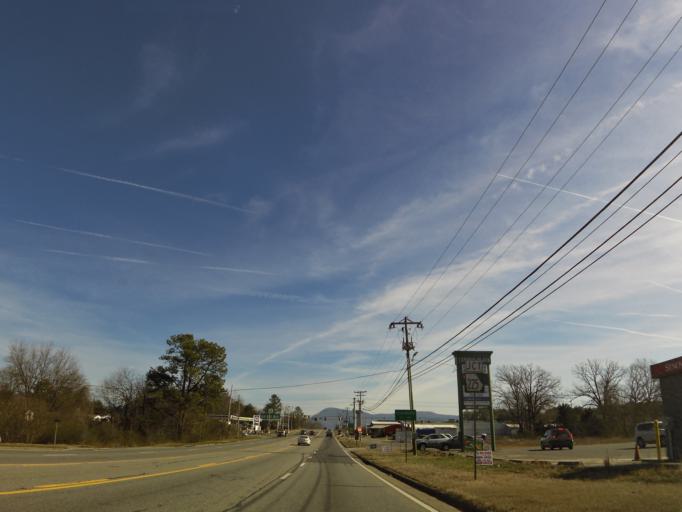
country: US
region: Georgia
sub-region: Murray County
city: Chatsworth
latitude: 34.7828
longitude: -84.8263
